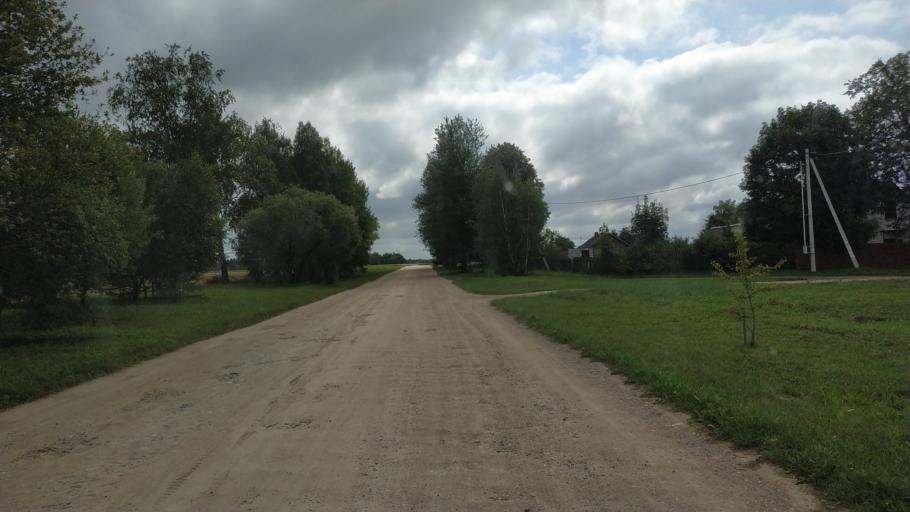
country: BY
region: Mogilev
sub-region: Mahilyowski Rayon
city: Kadino
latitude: 53.8465
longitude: 30.4750
